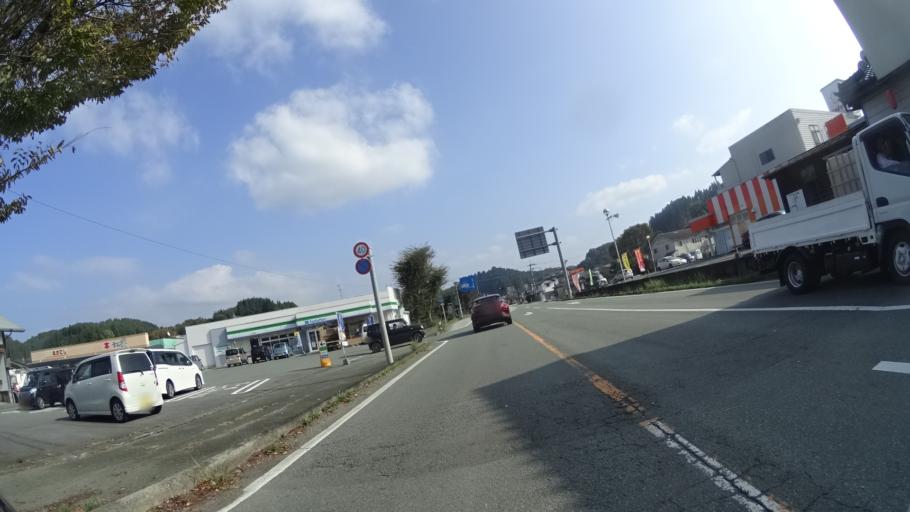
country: JP
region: Oita
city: Tsukawaki
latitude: 33.1237
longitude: 131.0630
